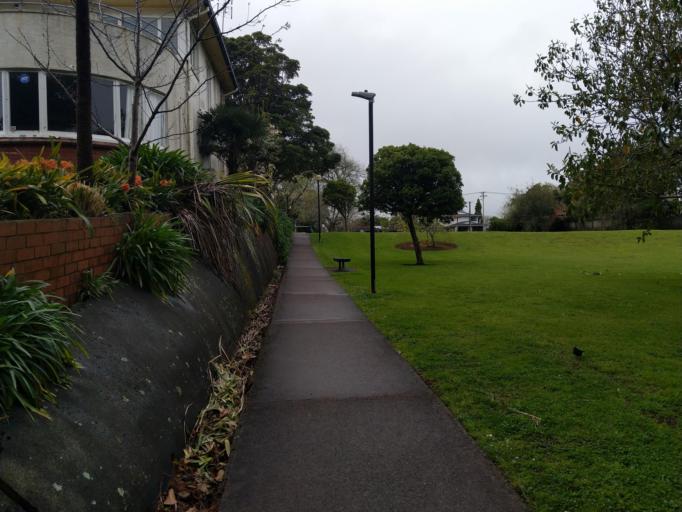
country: NZ
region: Auckland
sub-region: Auckland
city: Auckland
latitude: -36.8927
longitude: 174.7643
